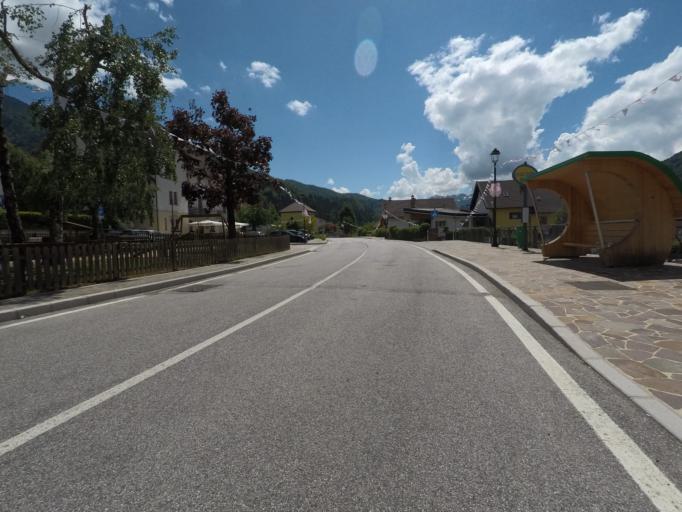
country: IT
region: Friuli Venezia Giulia
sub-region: Provincia di Udine
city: Ovaro
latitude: 46.4835
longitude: 12.8660
